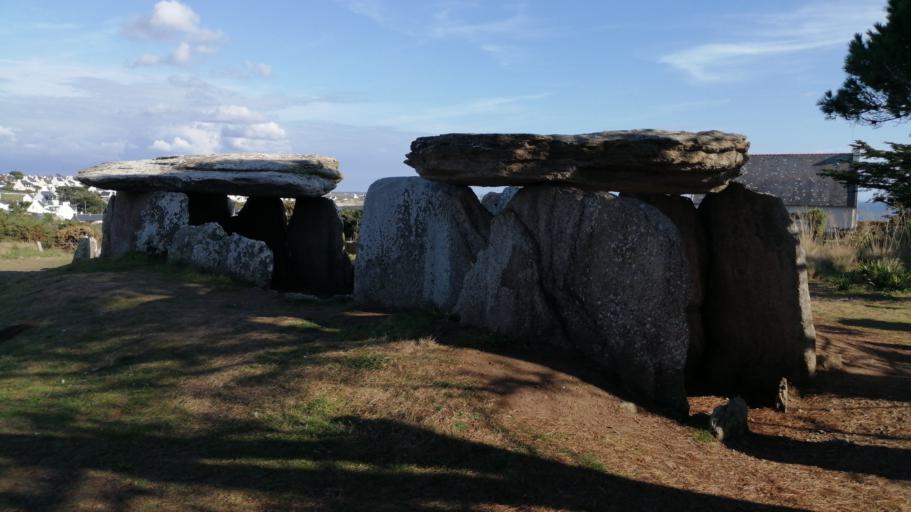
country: FR
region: Brittany
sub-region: Departement du Finistere
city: Plouhinec
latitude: 47.9863
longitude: -4.4657
